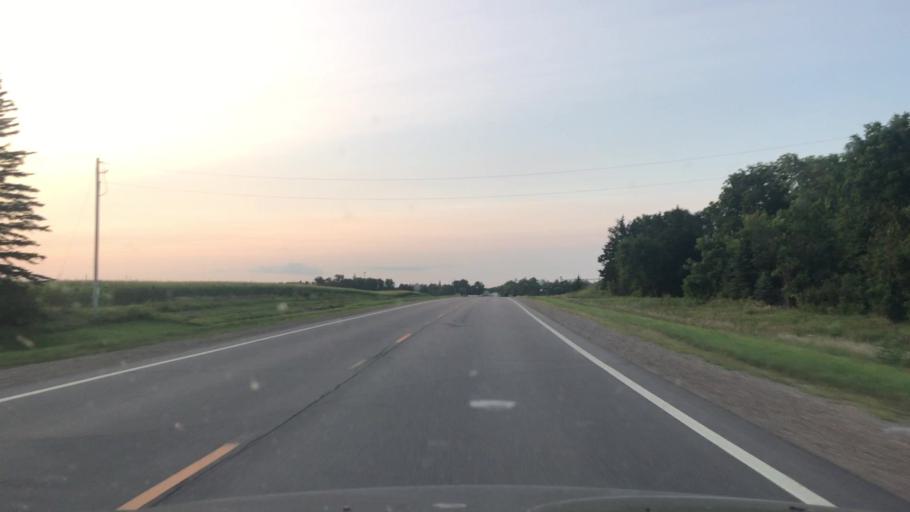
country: US
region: Minnesota
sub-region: Redwood County
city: Redwood Falls
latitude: 44.5174
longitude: -95.1181
